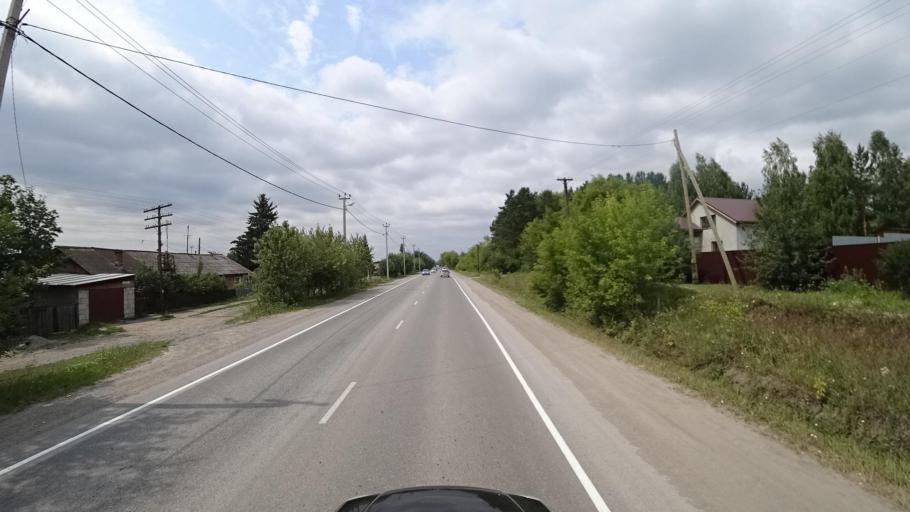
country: RU
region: Sverdlovsk
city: Obukhovskoye
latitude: 56.8461
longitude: 62.6534
